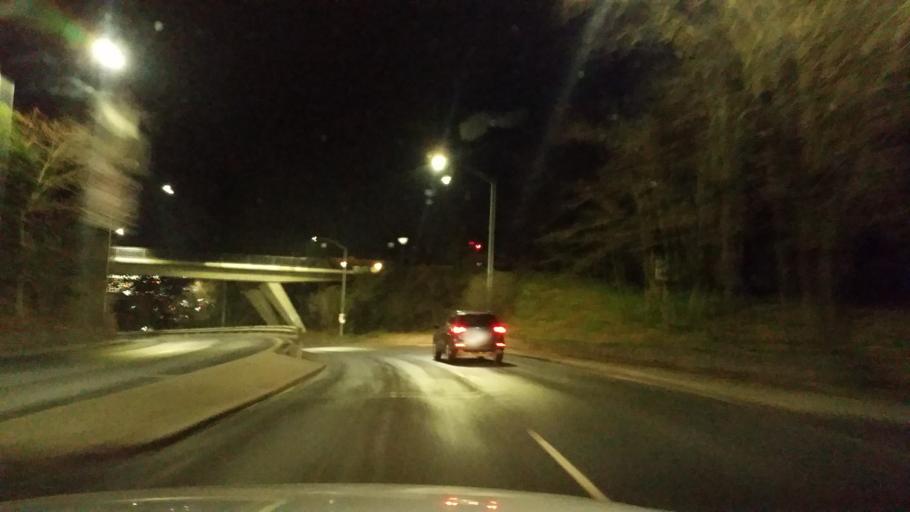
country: US
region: Washington
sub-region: Spokane County
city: Spokane
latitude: 47.6454
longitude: -117.4168
